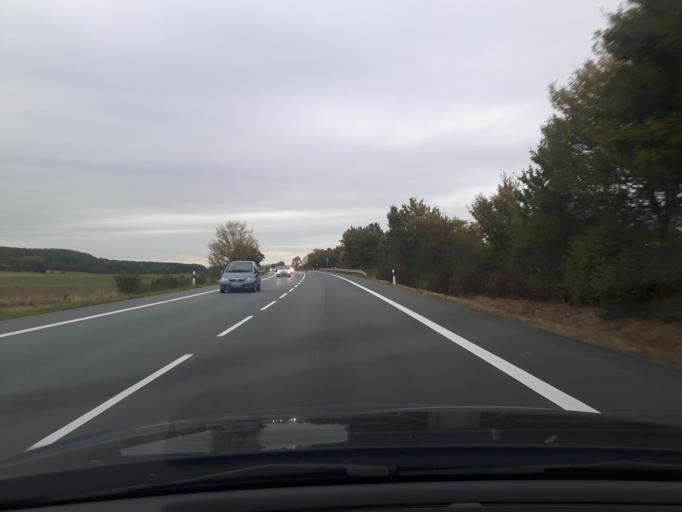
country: DE
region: Hesse
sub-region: Regierungsbezirk Giessen
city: Grossen Buseck
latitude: 50.5549
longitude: 8.7654
